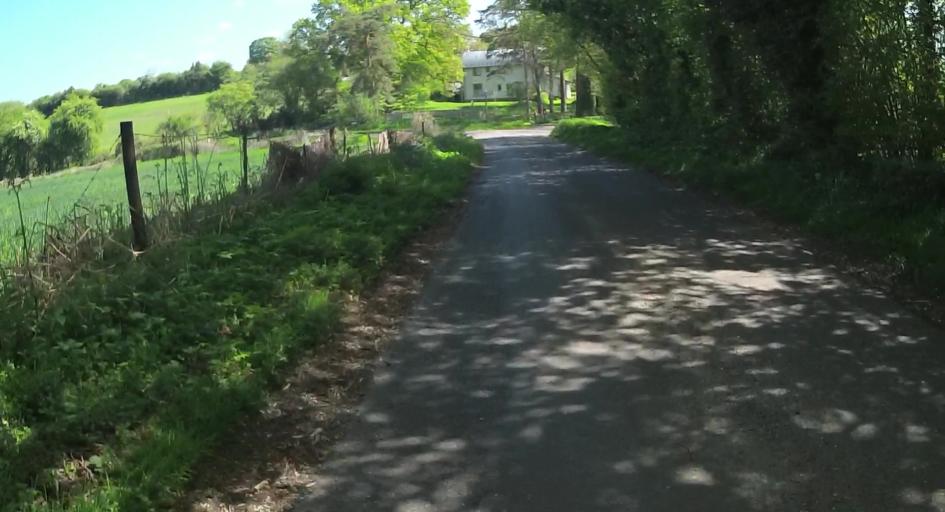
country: GB
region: England
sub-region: Hampshire
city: Four Marks
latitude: 51.1207
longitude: -1.0921
